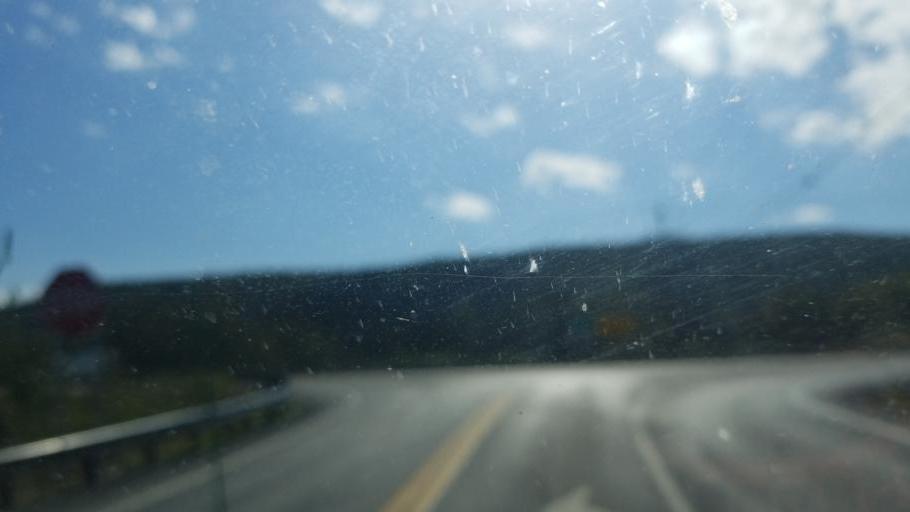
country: US
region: Pennsylvania
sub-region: Bedford County
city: Bedford
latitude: 40.0477
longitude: -78.5502
